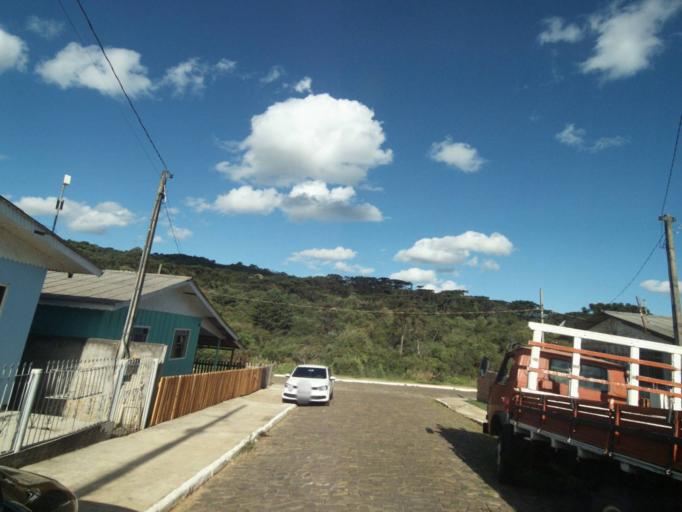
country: BR
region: Parana
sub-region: Uniao Da Vitoria
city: Uniao da Vitoria
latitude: -26.1607
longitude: -51.5326
